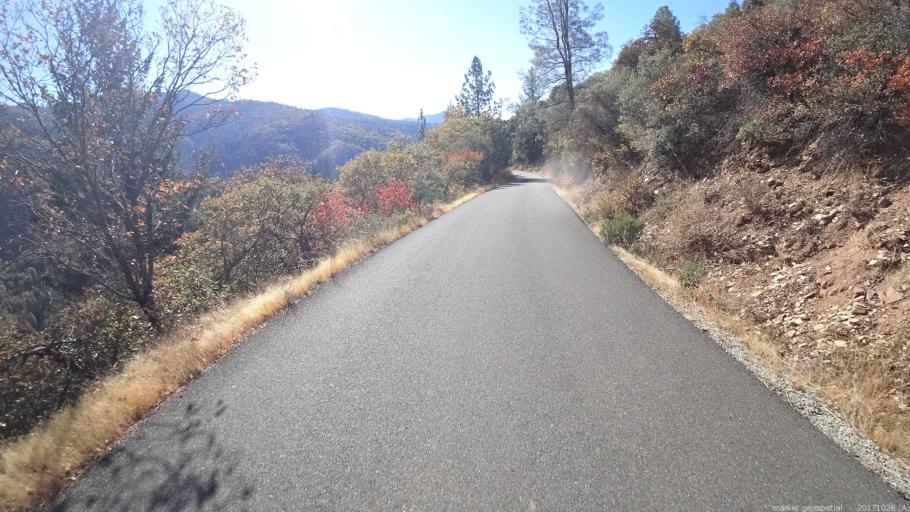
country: US
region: California
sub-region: Trinity County
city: Lewiston
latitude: 40.8064
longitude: -122.6107
